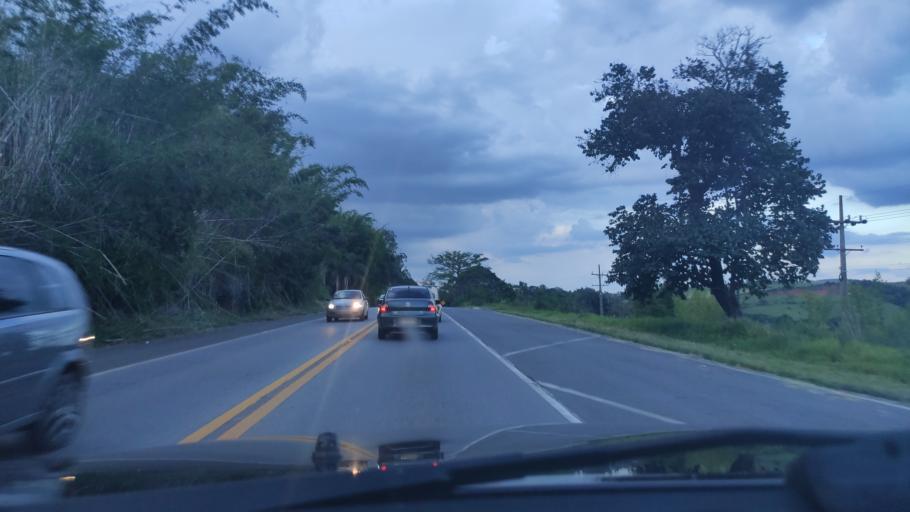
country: BR
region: Sao Paulo
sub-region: Braganca Paulista
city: Braganca Paulista
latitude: -22.8978
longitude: -46.5427
